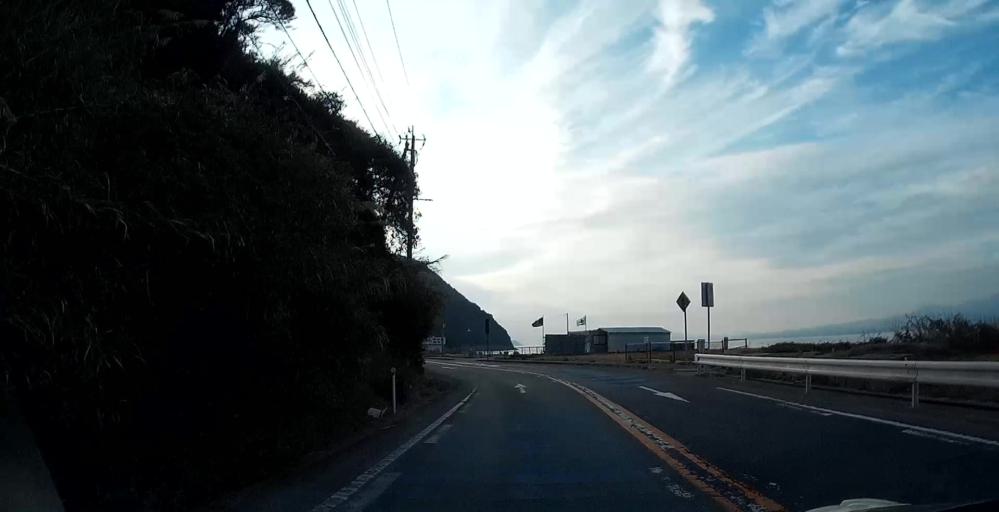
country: JP
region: Nagasaki
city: Shimabara
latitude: 32.6283
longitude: 130.4558
